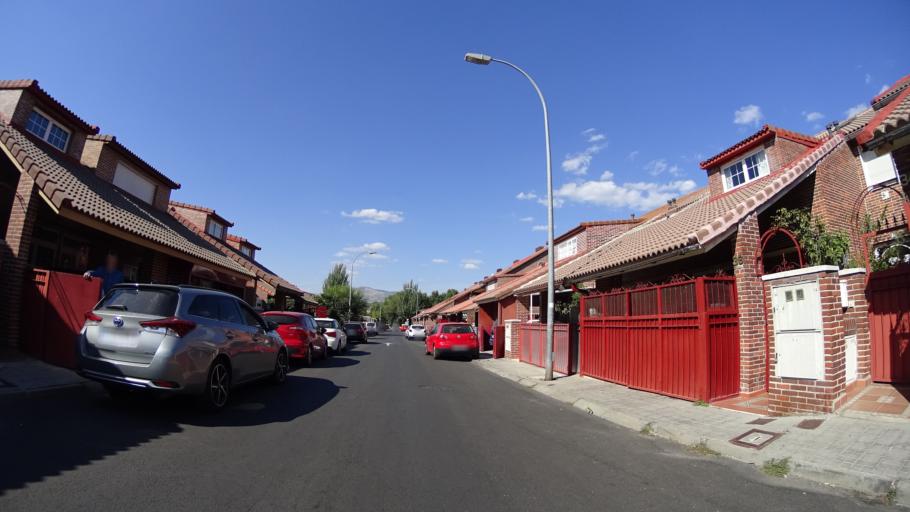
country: ES
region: Madrid
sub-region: Provincia de Madrid
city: Collado-Villalba
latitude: 40.6218
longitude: -4.0146
